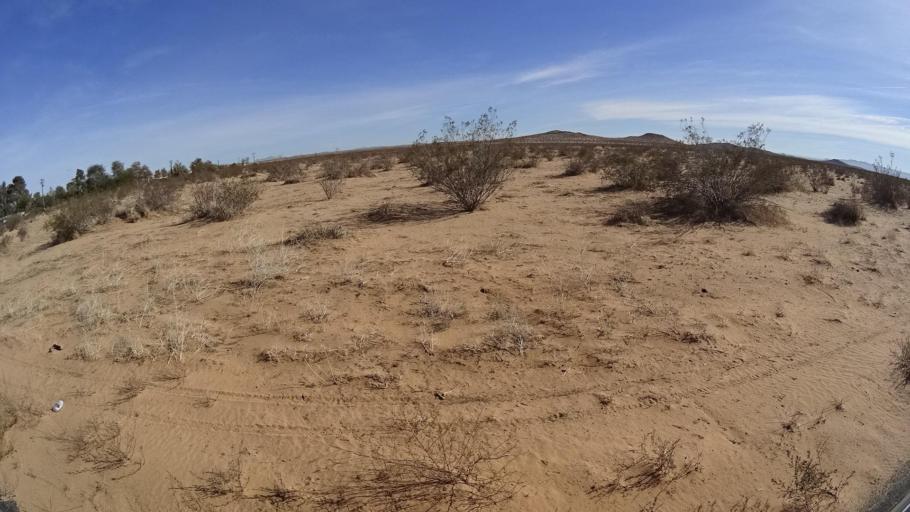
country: US
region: California
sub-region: Kern County
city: North Edwards
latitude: 35.0866
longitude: -117.7927
